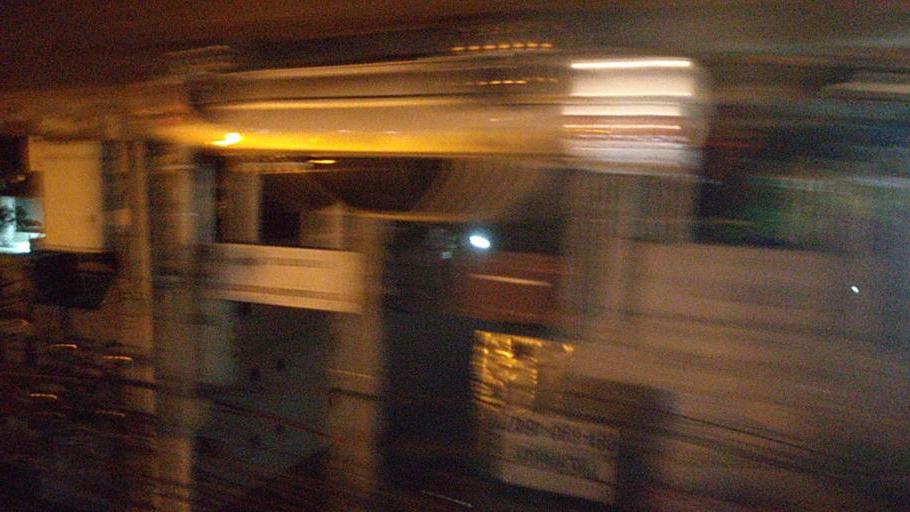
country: TH
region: Bangkok
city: Sai Mai
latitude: 13.9328
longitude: 100.6837
